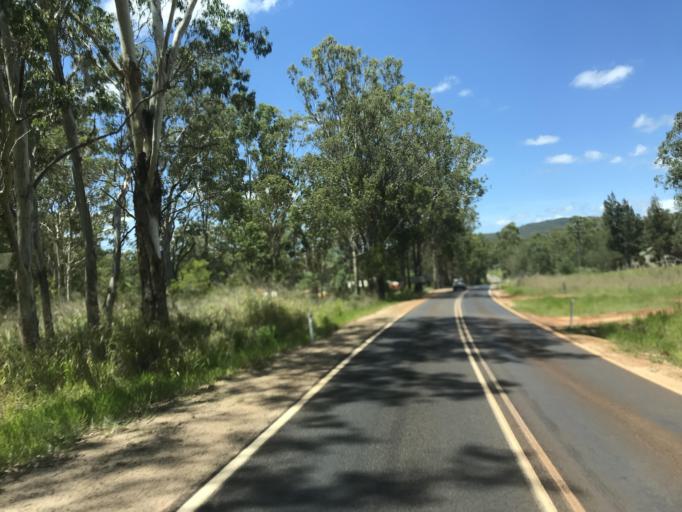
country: AU
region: Queensland
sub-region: Tablelands
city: Atherton
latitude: -17.4171
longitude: 145.3926
